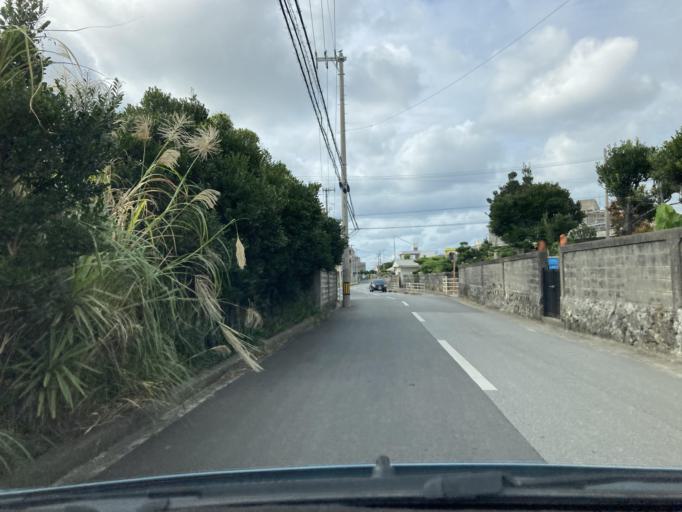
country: JP
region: Okinawa
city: Itoman
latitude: 26.1031
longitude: 127.6925
